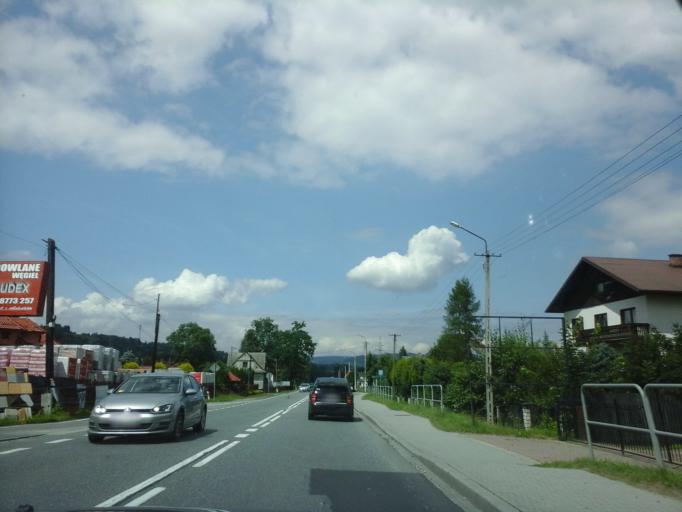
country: PL
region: Lesser Poland Voivodeship
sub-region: Powiat suski
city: Juszczyn
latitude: 49.6978
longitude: 19.7052
